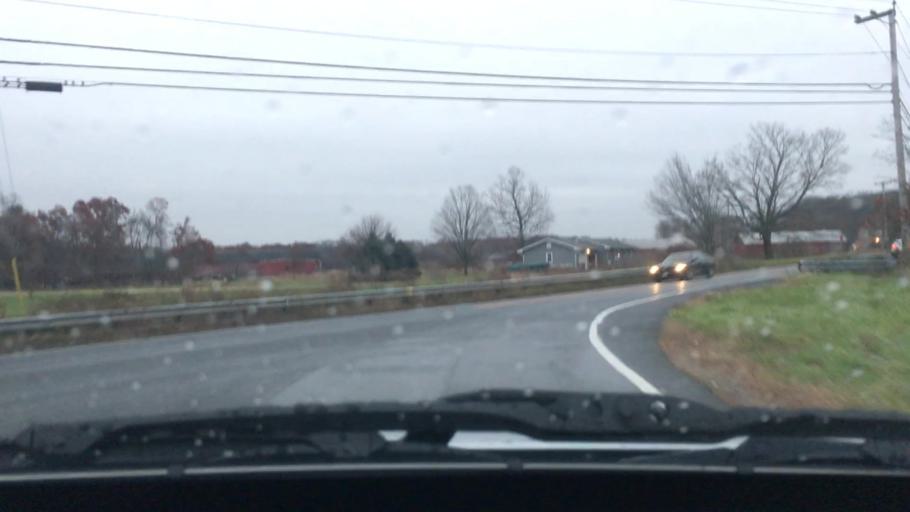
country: US
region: Massachusetts
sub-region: Hampden County
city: Southwick
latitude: 42.0779
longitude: -72.7687
